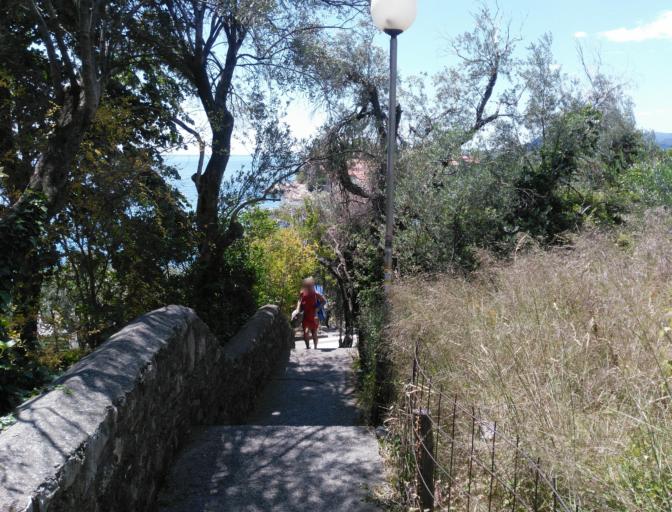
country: ME
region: Budva
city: Budva
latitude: 42.2558
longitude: 18.8961
